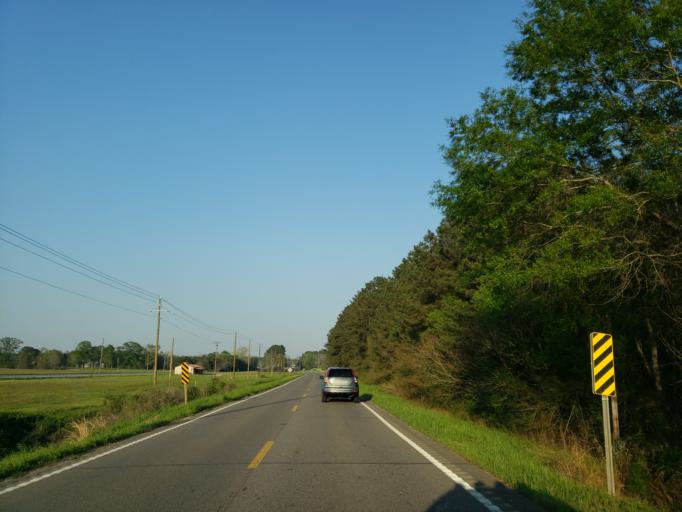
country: US
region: Mississippi
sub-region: Lauderdale County
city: Marion
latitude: 32.3964
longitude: -88.6147
